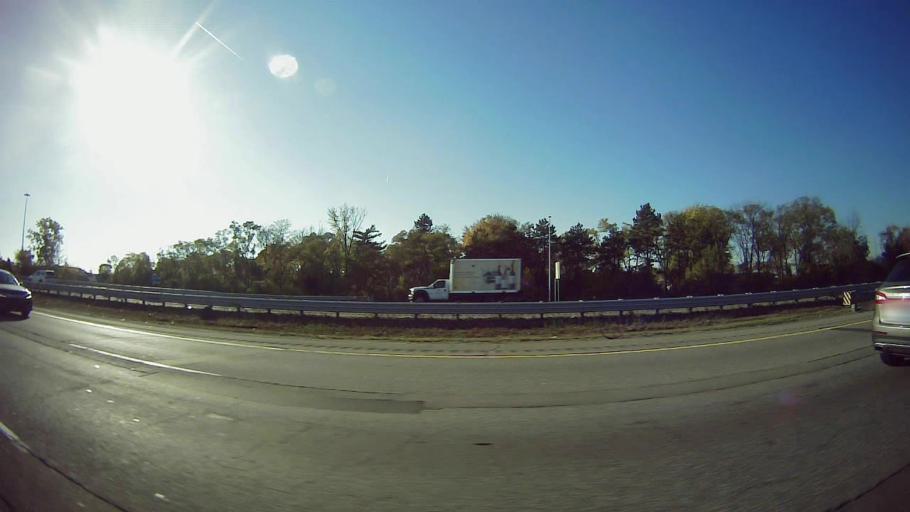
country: US
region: Michigan
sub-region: Oakland County
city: Madison Heights
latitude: 42.5079
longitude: -83.1148
